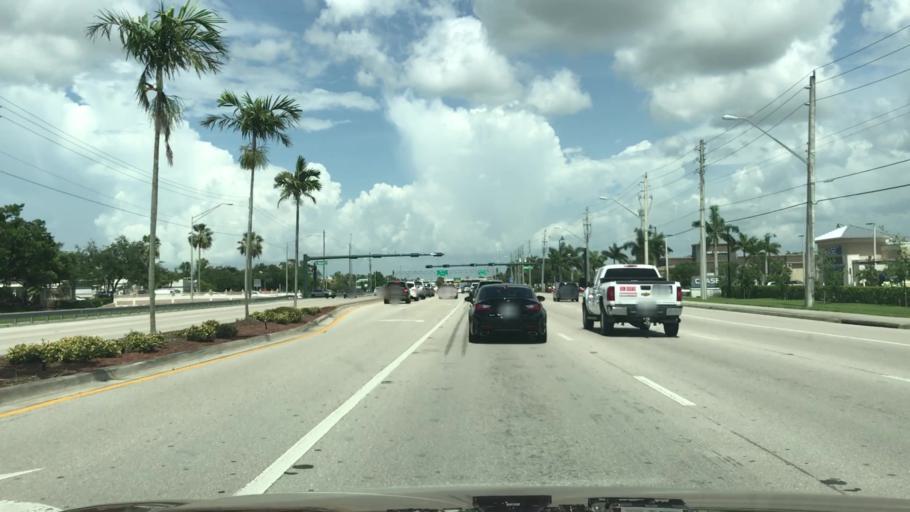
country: US
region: Florida
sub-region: Collier County
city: Vineyards
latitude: 26.2727
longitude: -81.7493
